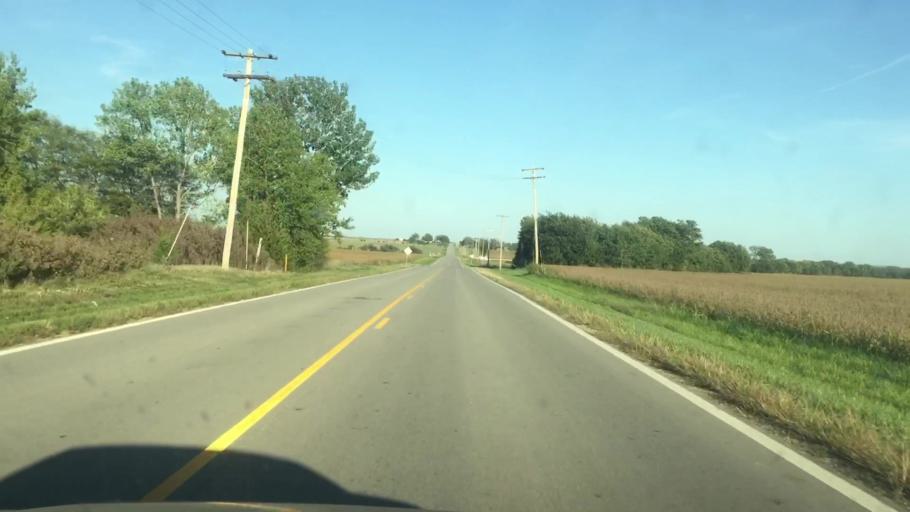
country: US
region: Kansas
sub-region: Brown County
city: Horton
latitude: 39.5876
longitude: -95.6069
